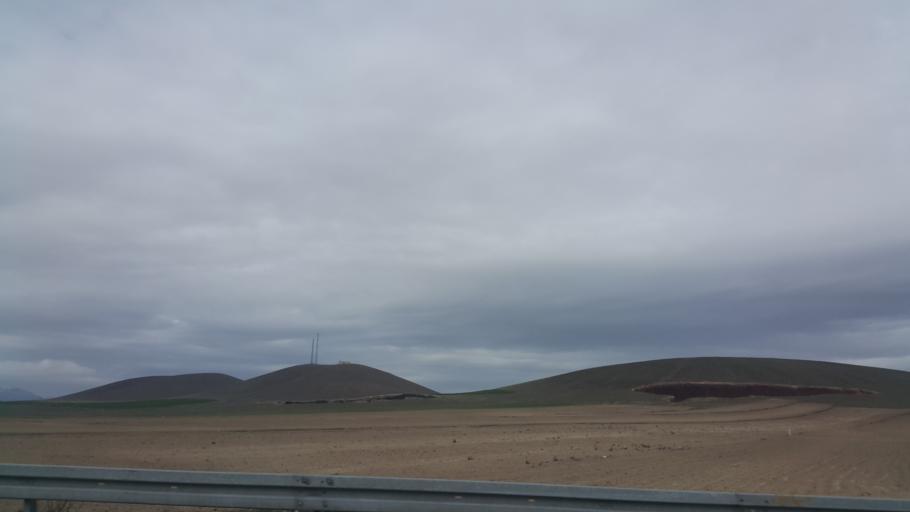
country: TR
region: Aksaray
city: Taspinar
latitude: 37.9435
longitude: 34.0947
